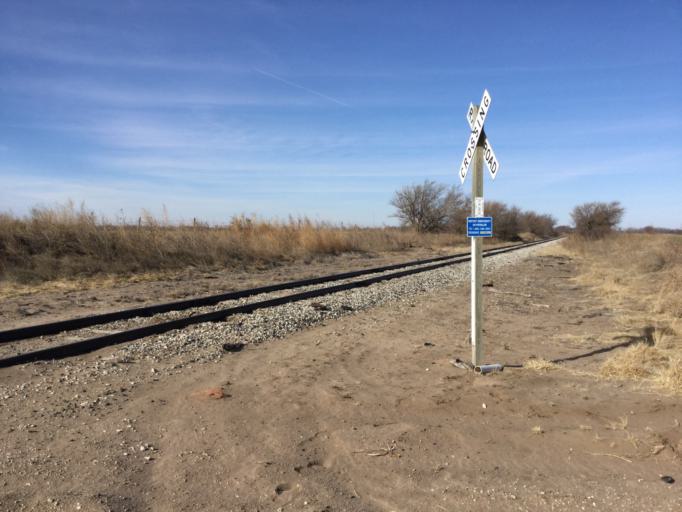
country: US
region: Kansas
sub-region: Rice County
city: Sterling
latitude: 38.2223
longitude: -98.2523
